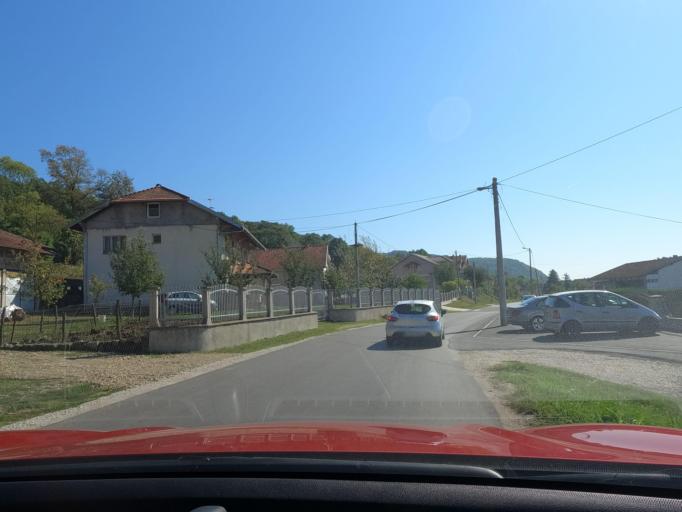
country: RS
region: Central Serbia
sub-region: Raski Okrug
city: Kraljevo
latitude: 43.7444
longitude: 20.7269
